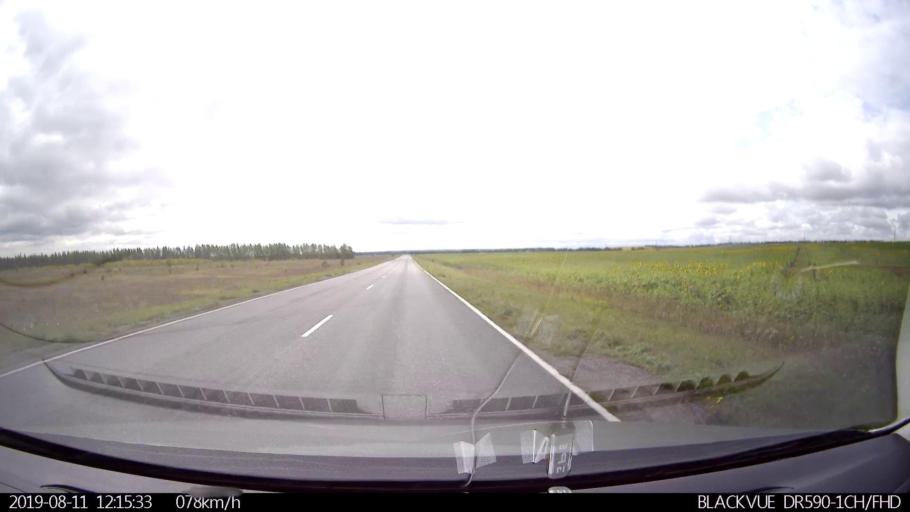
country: RU
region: Ulyanovsk
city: Ignatovka
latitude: 53.9406
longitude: 47.9677
